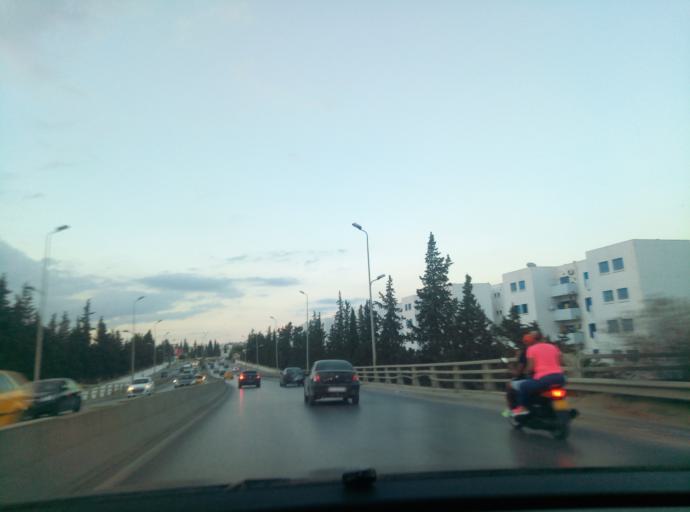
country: TN
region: Manouba
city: Manouba
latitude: 36.8111
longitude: 10.1202
